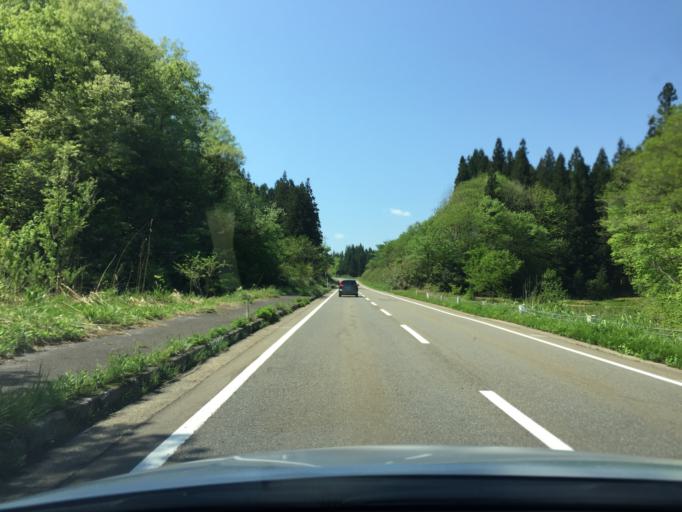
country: JP
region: Niigata
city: Kamo
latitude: 37.5968
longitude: 139.0945
